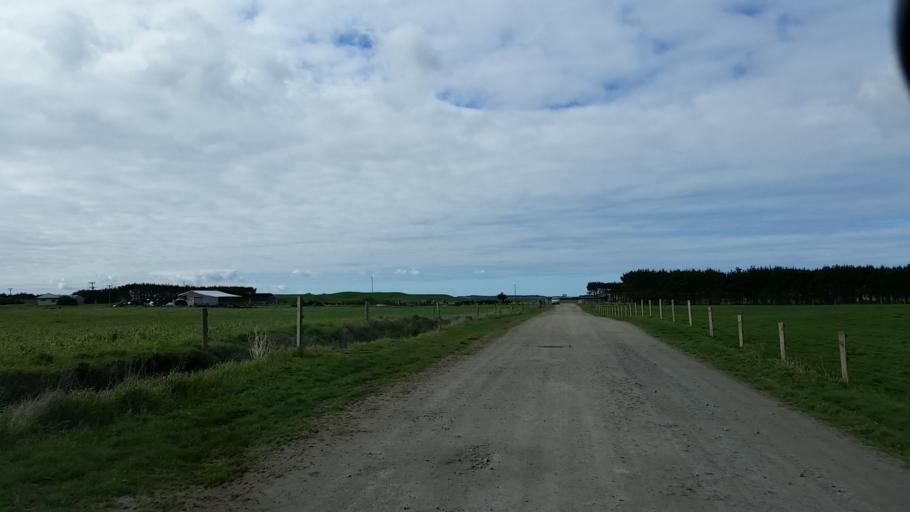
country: NZ
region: Taranaki
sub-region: South Taranaki District
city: Patea
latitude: -39.8253
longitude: 174.6563
